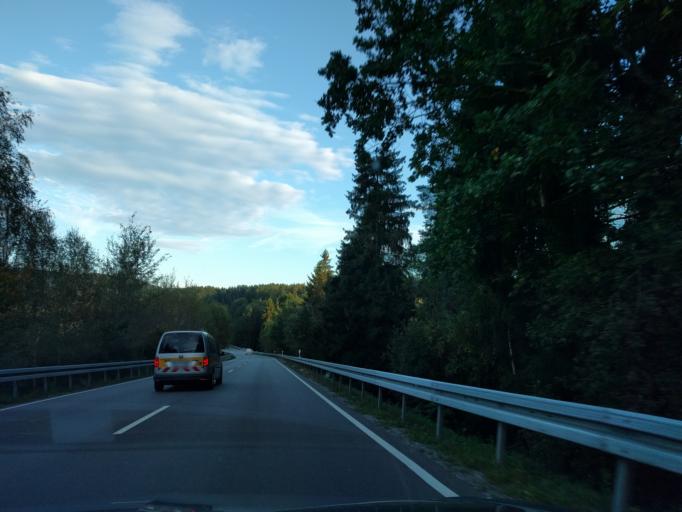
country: DE
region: Bavaria
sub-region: Lower Bavaria
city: Viechtach
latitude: 49.0582
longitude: 12.9101
